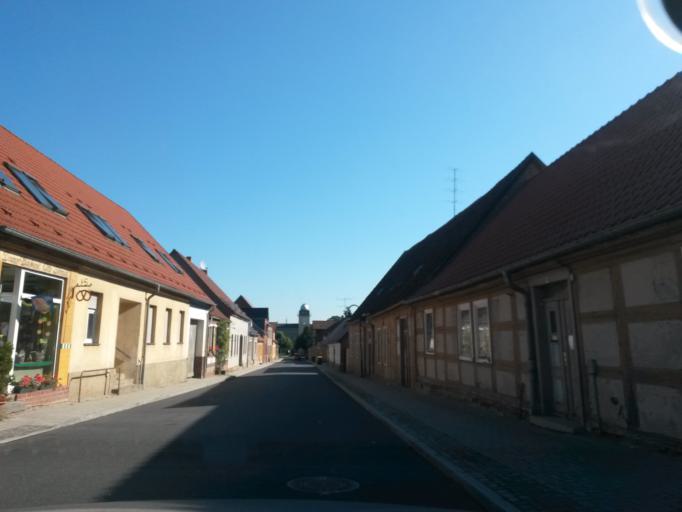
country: DE
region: Brandenburg
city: Angermunde
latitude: 53.0888
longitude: 13.9585
